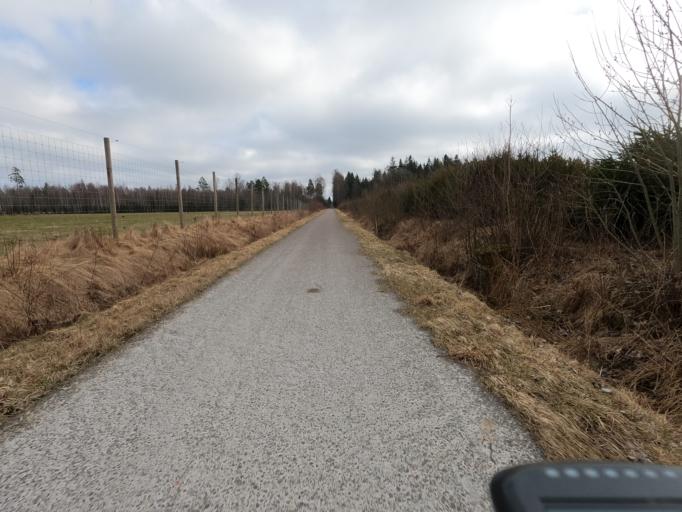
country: SE
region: Joenkoeping
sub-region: Varnamo Kommun
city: Rydaholm
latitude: 56.8608
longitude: 14.1742
